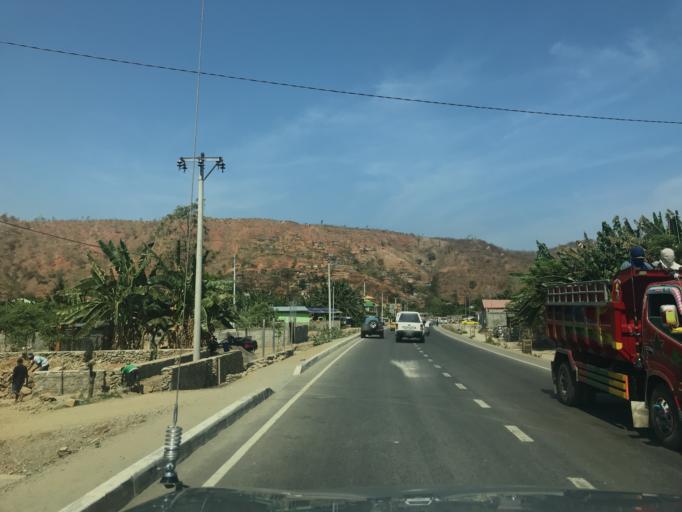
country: TL
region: Dili
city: Dili
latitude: -8.5621
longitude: 125.5281
